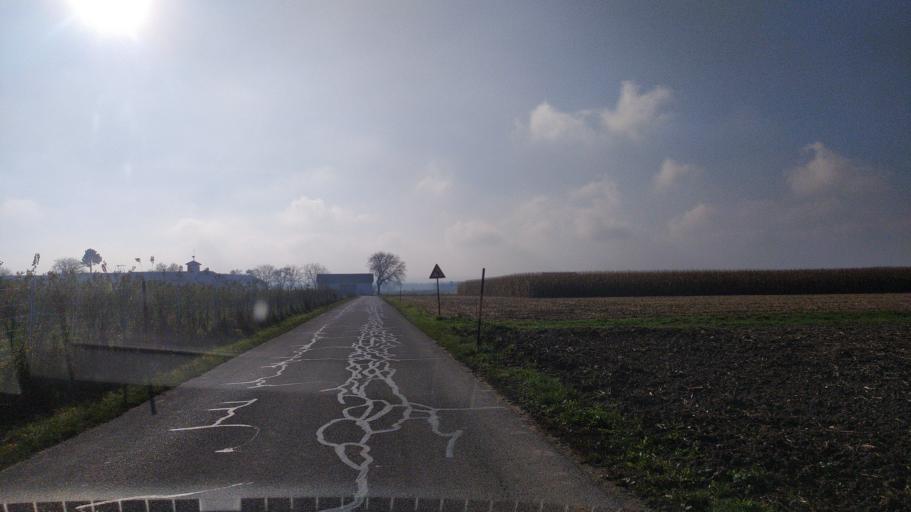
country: AT
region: Upper Austria
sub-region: Politischer Bezirk Perg
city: Perg
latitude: 48.1984
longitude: 14.6518
